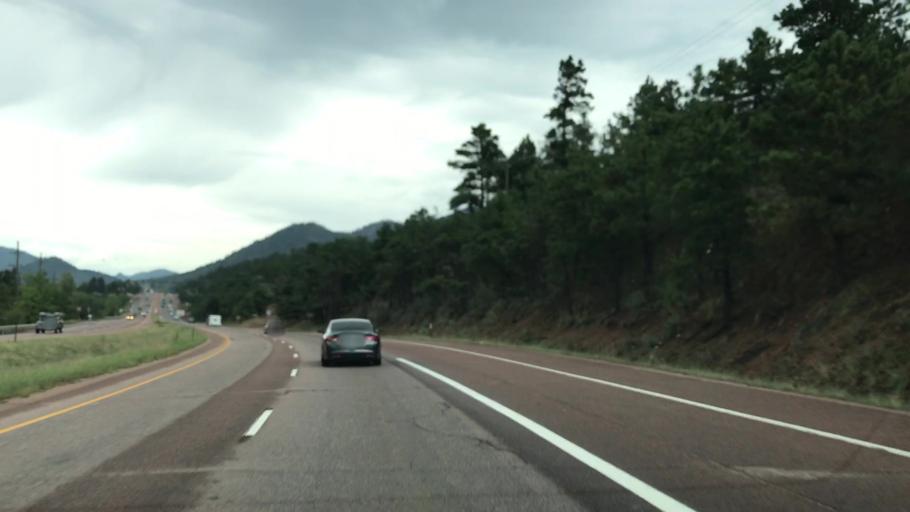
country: US
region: Colorado
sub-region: El Paso County
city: Cascade-Chipita Park
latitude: 38.9073
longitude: -104.9709
